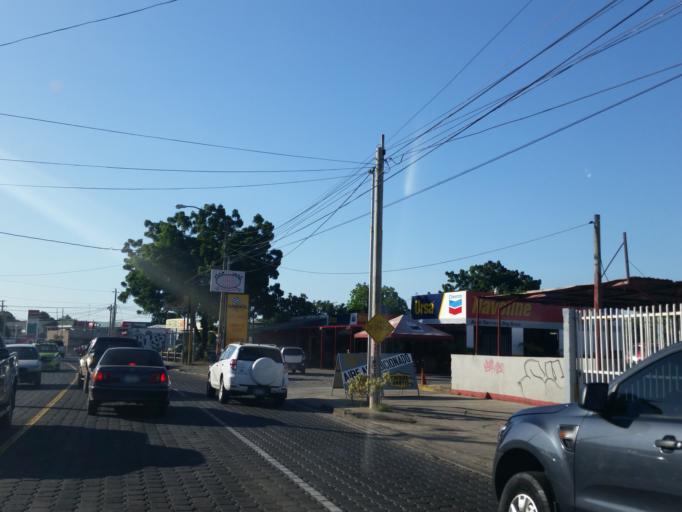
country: NI
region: Managua
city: Managua
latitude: 12.1374
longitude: -86.2885
